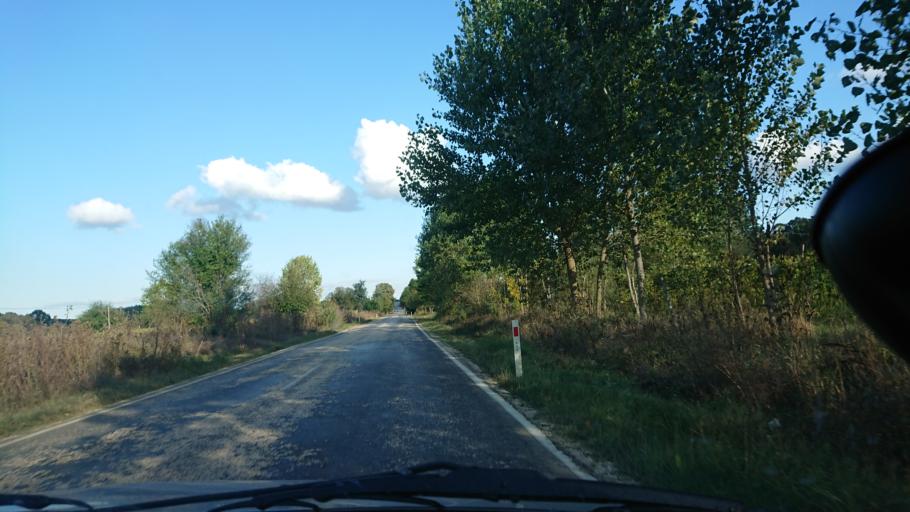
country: TR
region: Bilecik
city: Pazaryeri
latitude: 40.0151
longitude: 29.8434
